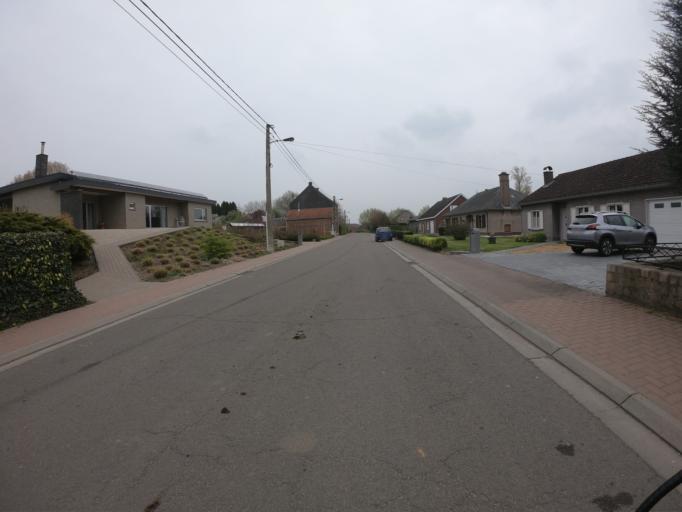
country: BE
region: Wallonia
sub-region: Province du Hainaut
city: Flobecq
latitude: 50.7390
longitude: 3.7498
